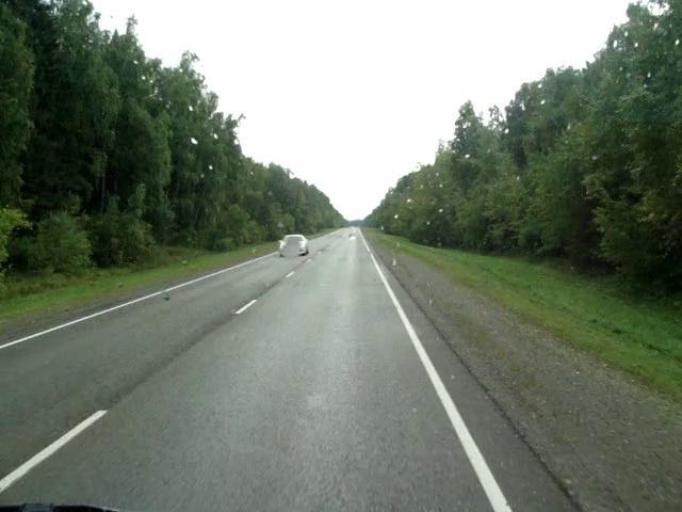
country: RU
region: Altai Krai
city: Shul'gin Log
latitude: 52.1964
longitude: 85.9005
